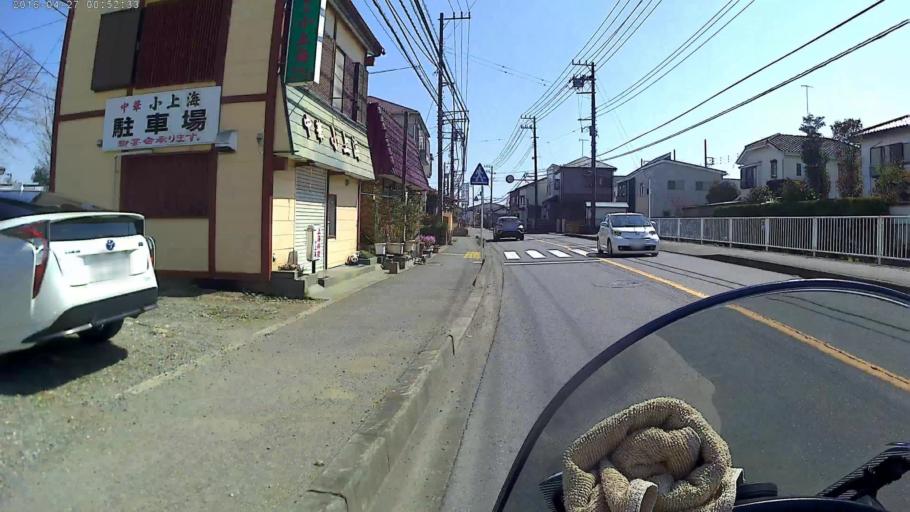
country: JP
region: Kanagawa
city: Chigasaki
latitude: 35.3618
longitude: 139.3891
